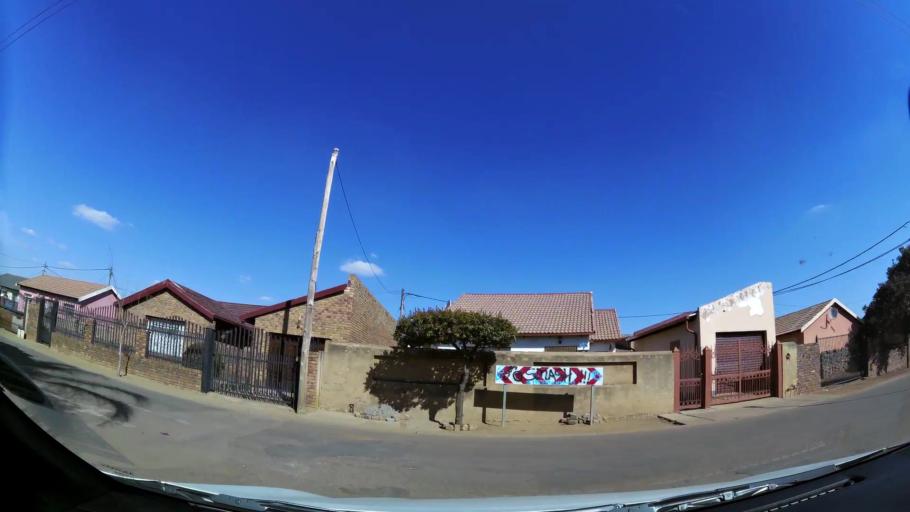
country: ZA
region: Gauteng
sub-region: City of Tshwane Metropolitan Municipality
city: Cullinan
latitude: -25.7159
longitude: 28.3950
